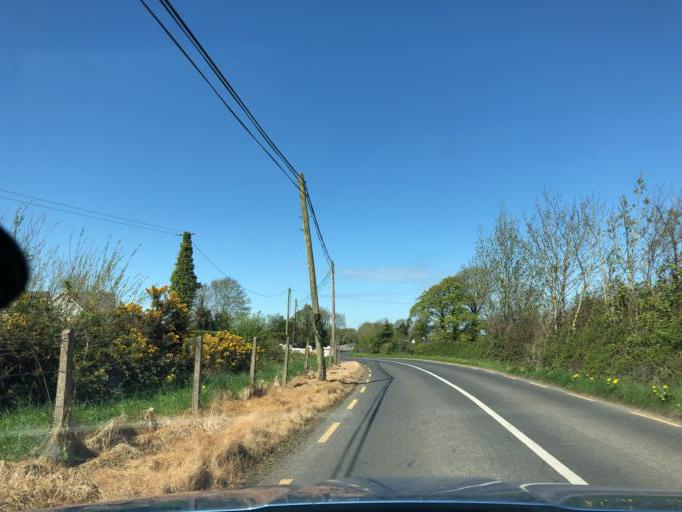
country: IE
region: Connaught
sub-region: County Galway
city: Portumna
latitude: 53.1262
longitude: -8.3388
